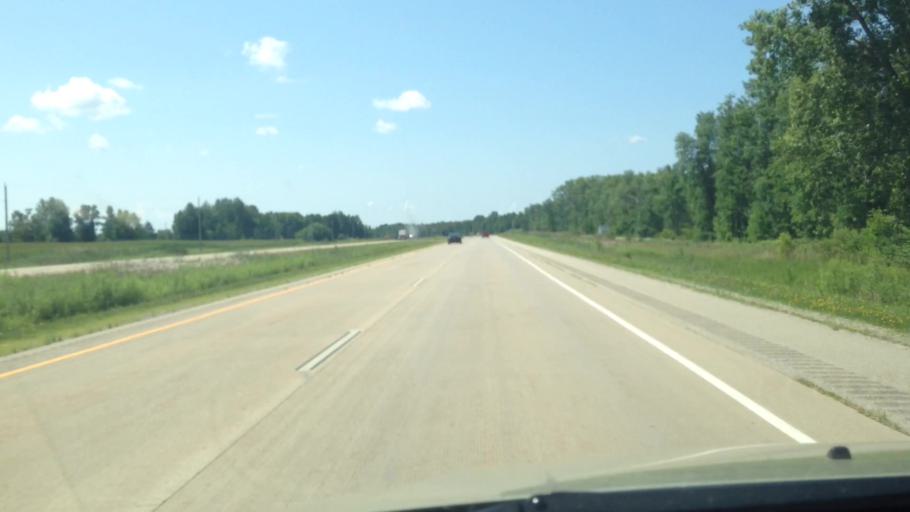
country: US
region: Wisconsin
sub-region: Oconto County
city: Oconto
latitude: 44.9757
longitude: -87.8677
